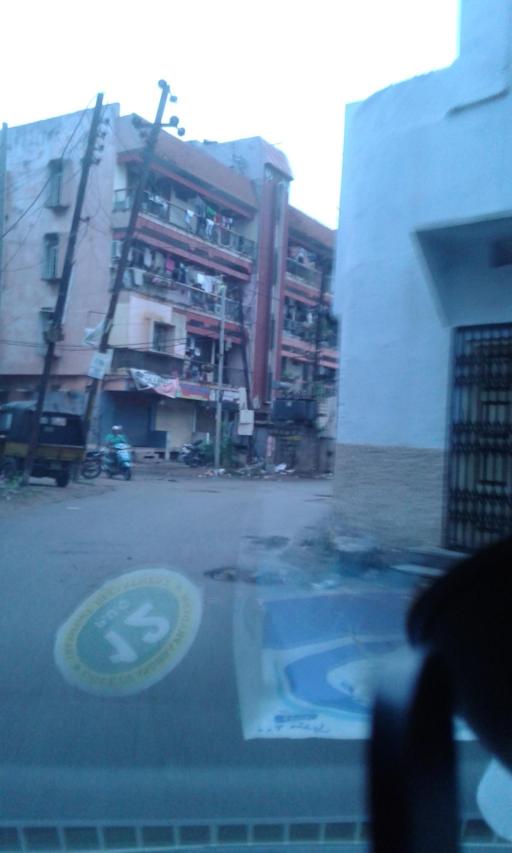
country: IN
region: Telangana
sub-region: Hyderabad
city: Hyderabad
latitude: 17.3759
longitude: 78.4882
